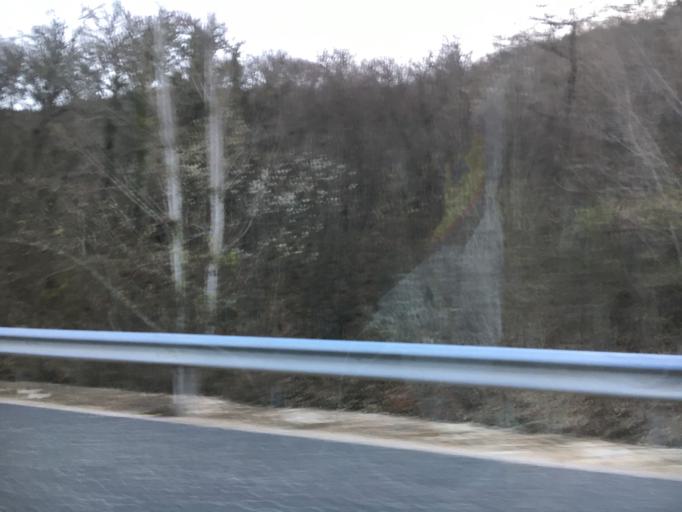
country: ES
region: Castille and Leon
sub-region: Provincia de Leon
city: Trabadelo
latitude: 42.6285
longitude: -6.8499
